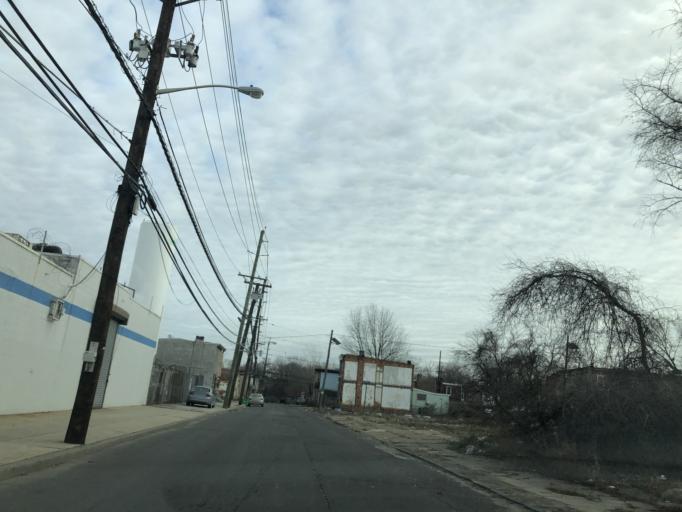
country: US
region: New Jersey
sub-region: Camden County
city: Camden
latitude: 39.9248
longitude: -75.1194
